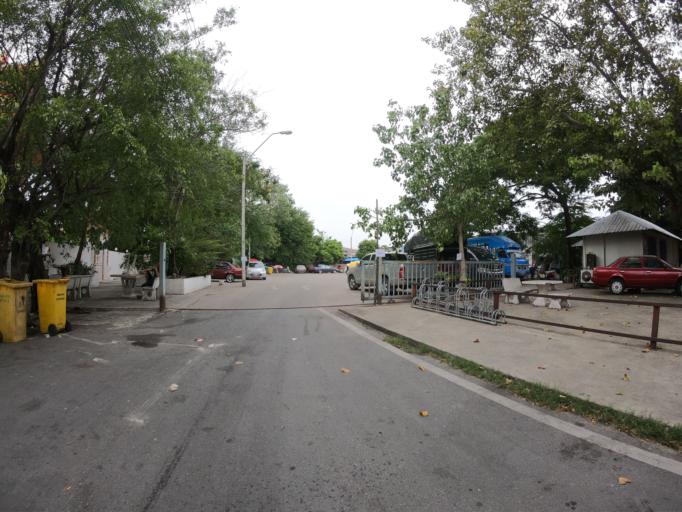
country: TH
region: Bangkok
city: Lat Phrao
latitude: 13.8271
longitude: 100.6177
